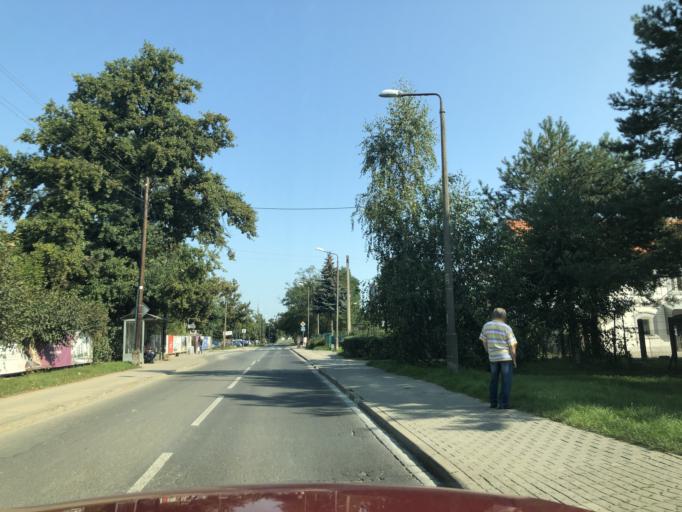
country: PL
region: Lower Silesian Voivodeship
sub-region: Powiat wroclawski
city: Smolec
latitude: 51.1663
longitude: 16.8984
